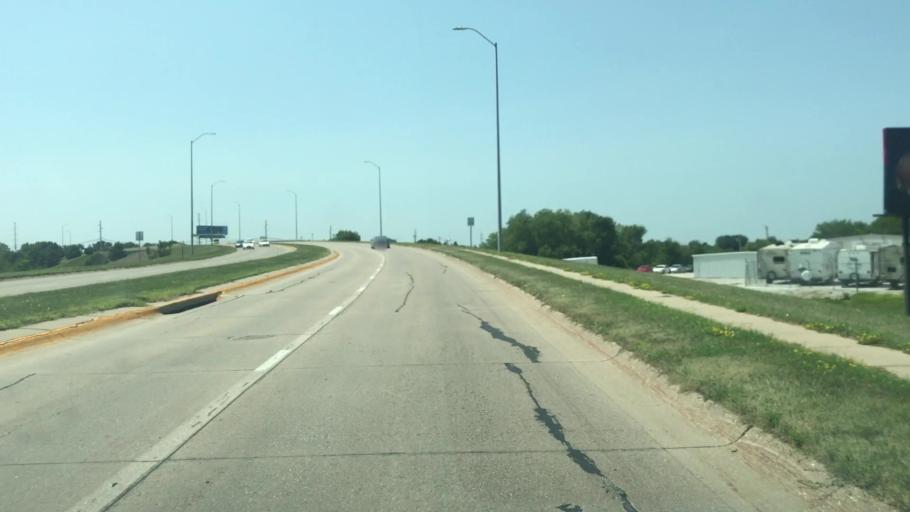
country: US
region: Nebraska
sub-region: Adams County
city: Hastings
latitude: 40.6075
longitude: -98.3892
